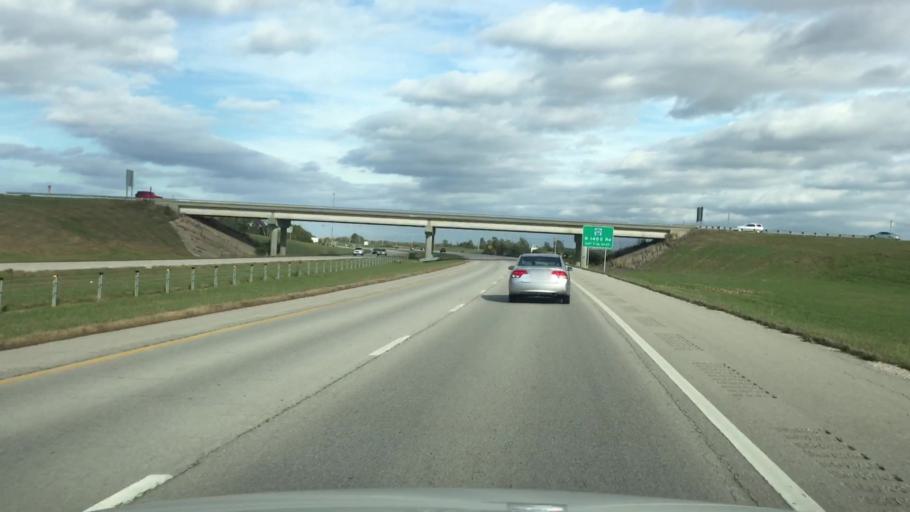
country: US
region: Kansas
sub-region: Douglas County
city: Eudora
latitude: 38.9326
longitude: -95.1005
